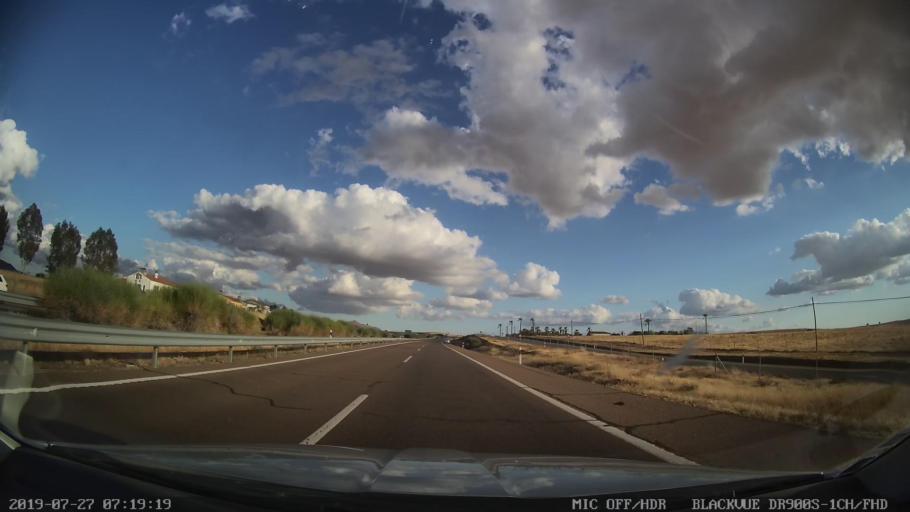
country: ES
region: Extremadura
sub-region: Provincia de Caceres
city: Trujillo
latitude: 39.4010
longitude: -5.8893
